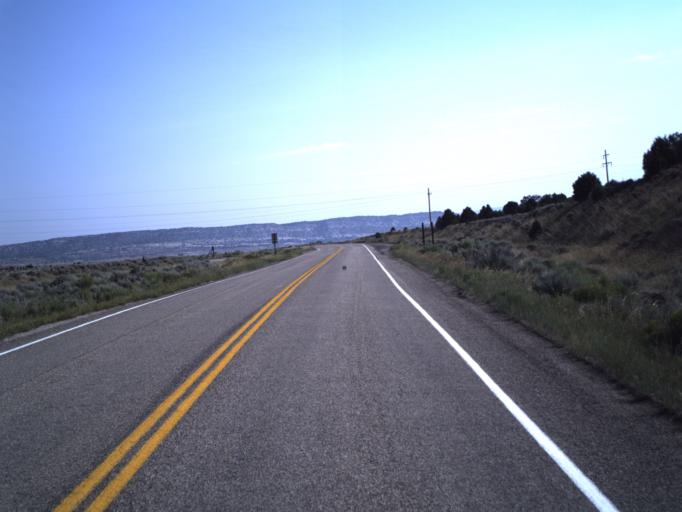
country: US
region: Utah
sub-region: Daggett County
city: Manila
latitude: 40.9575
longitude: -109.4708
